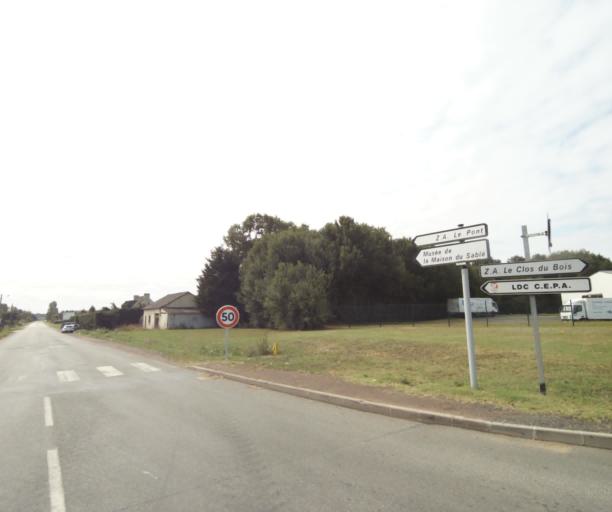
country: FR
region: Pays de la Loire
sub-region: Departement de la Sarthe
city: Sable-sur-Sarthe
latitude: 47.8261
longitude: -0.3116
